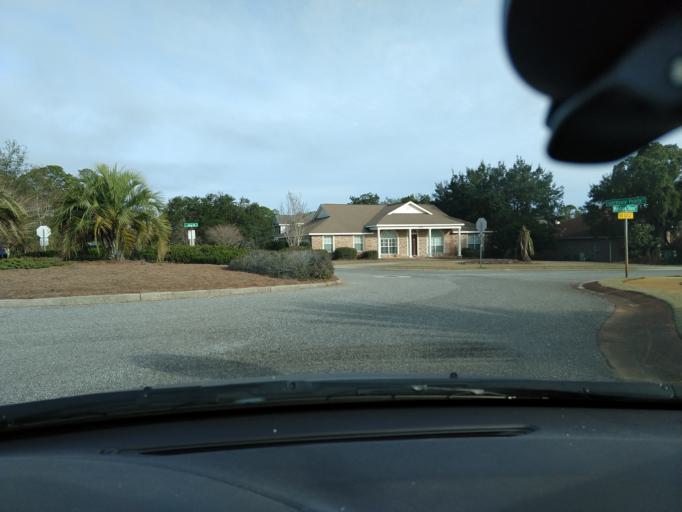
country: US
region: Florida
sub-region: Santa Rosa County
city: Woodlawn Beach
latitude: 30.3968
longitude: -86.9525
